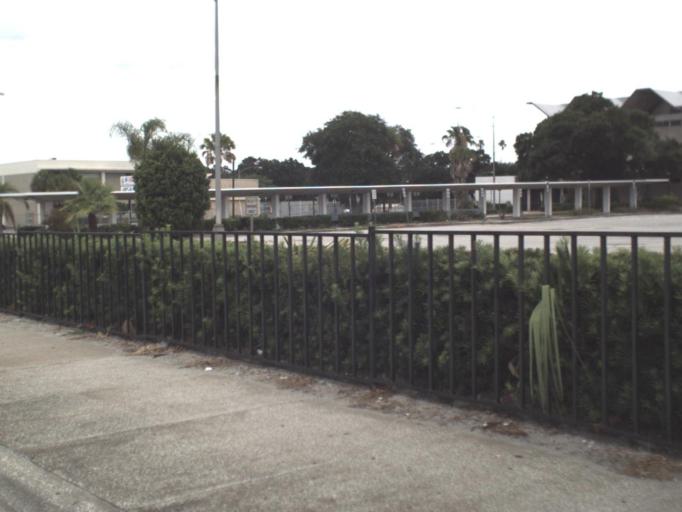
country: US
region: Florida
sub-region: Hillsborough County
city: Tampa
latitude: 27.9962
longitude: -82.4358
